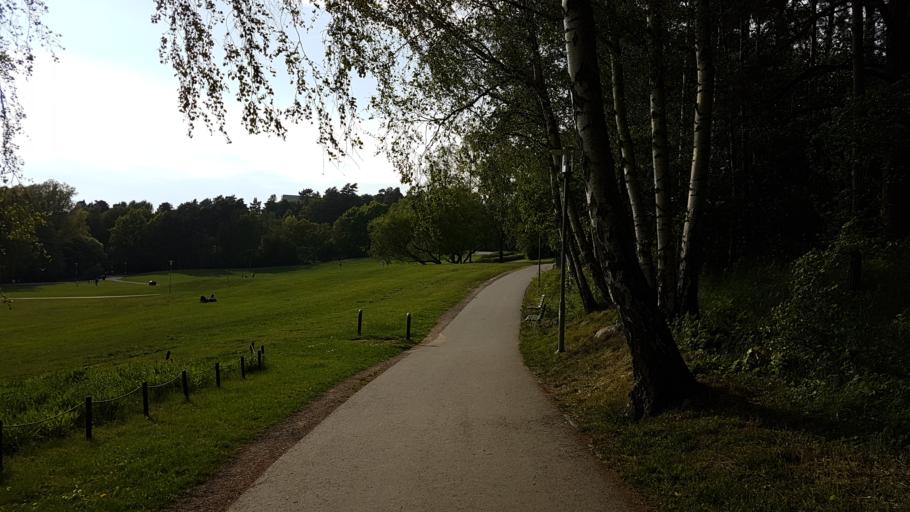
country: SE
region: Stockholm
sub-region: Solna Kommun
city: Rasunda
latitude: 59.3724
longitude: 17.9751
